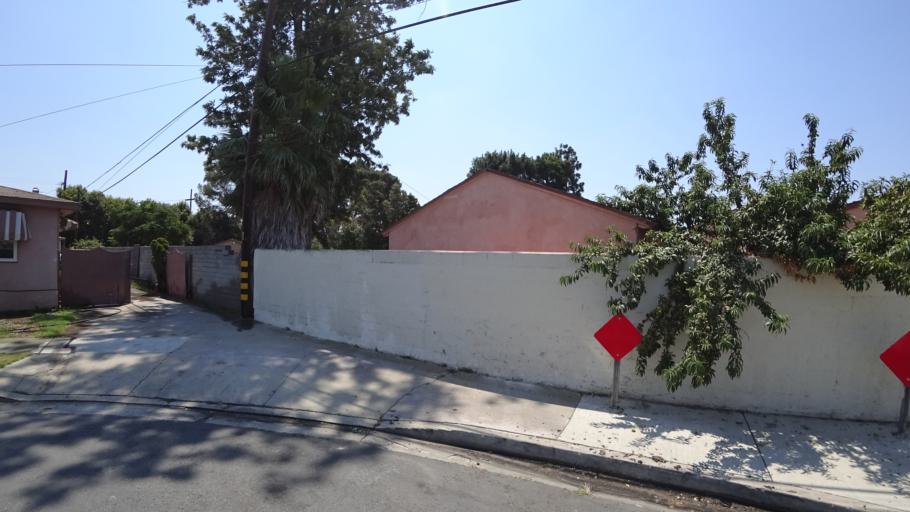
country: US
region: California
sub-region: Los Angeles County
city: Westmont
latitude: 33.9509
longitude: -118.3232
